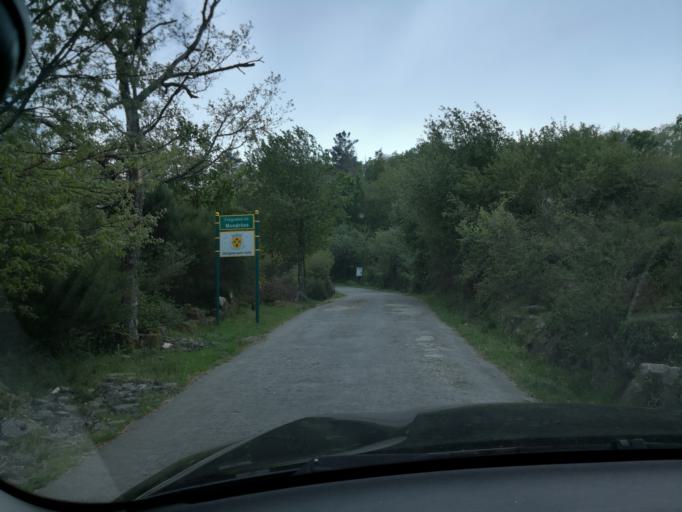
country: PT
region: Vila Real
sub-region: Vila Real
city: Vila Real
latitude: 41.2946
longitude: -7.8048
